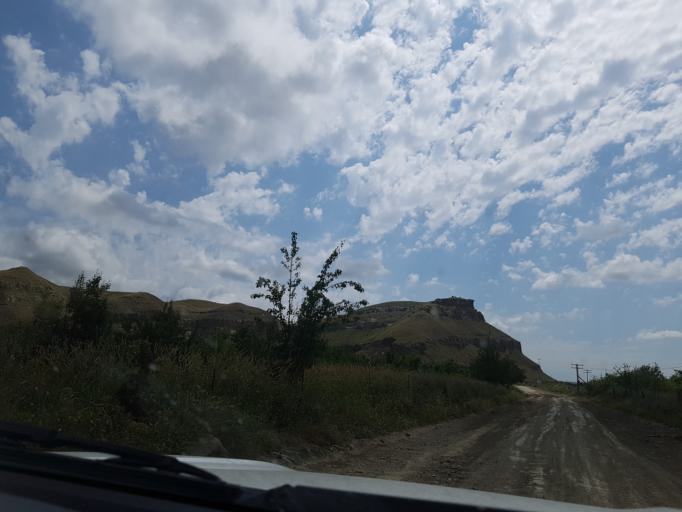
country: TM
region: Ahal
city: Baharly
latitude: 38.2230
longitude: 56.8957
